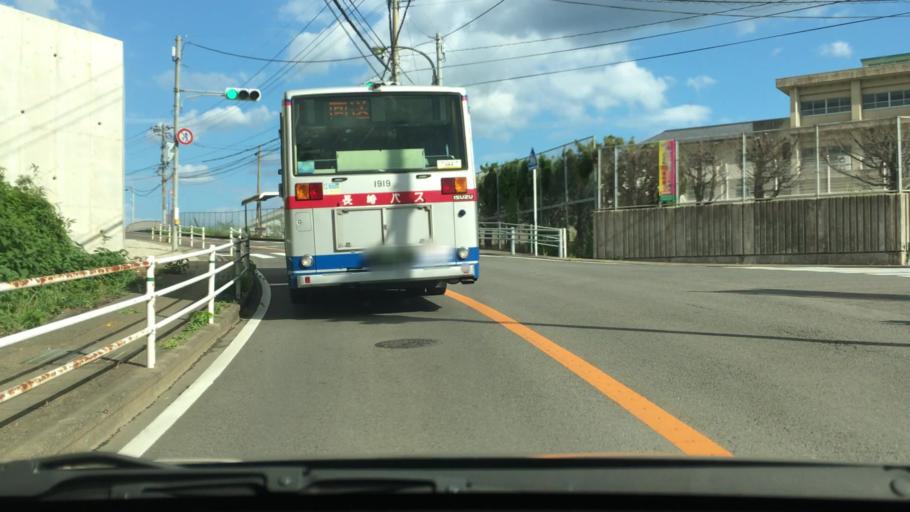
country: JP
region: Nagasaki
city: Togitsu
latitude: 32.8246
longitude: 129.7563
